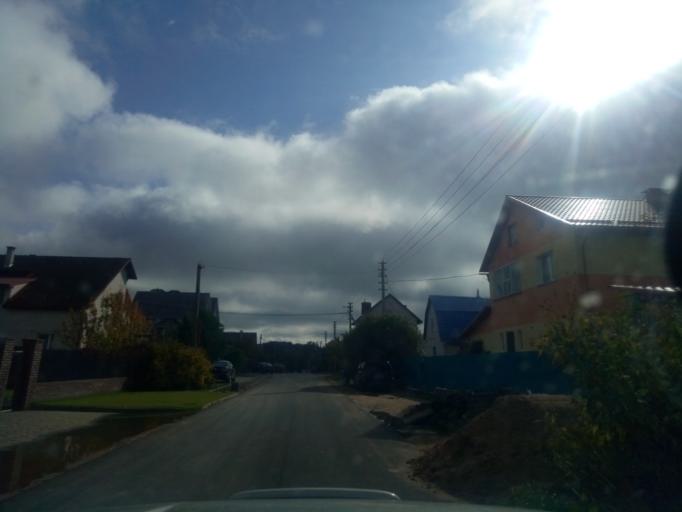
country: BY
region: Minsk
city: Zaslawye
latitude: 54.0004
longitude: 27.2702
